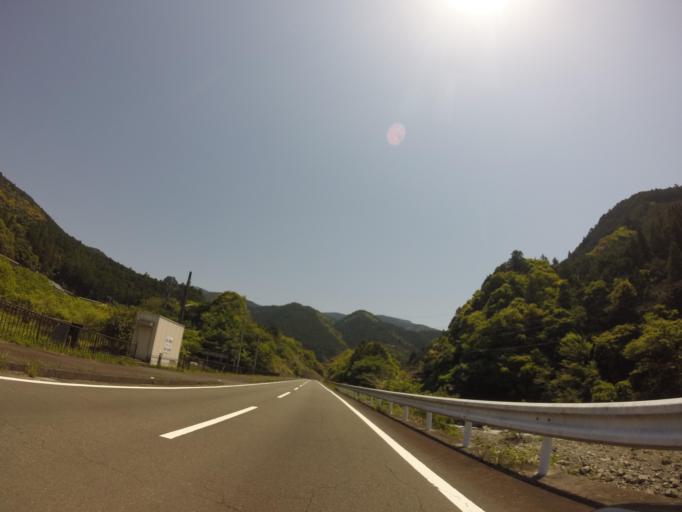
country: JP
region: Shizuoka
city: Shizuoka-shi
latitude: 35.0909
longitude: 138.2390
